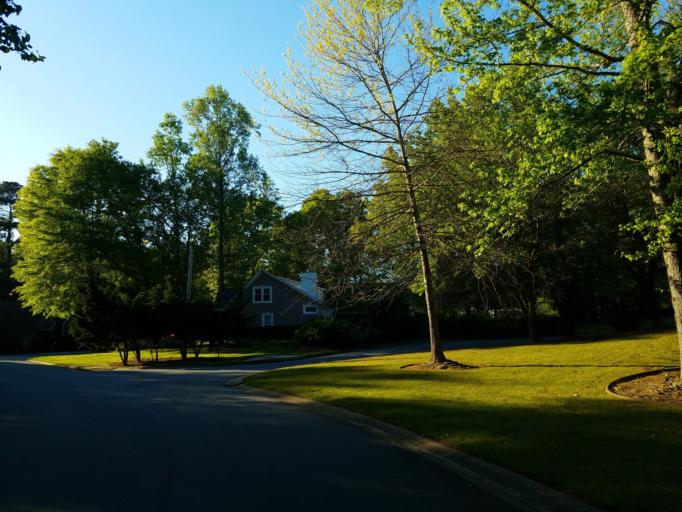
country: US
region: Georgia
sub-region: Cobb County
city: Powder Springs
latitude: 33.9187
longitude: -84.6426
